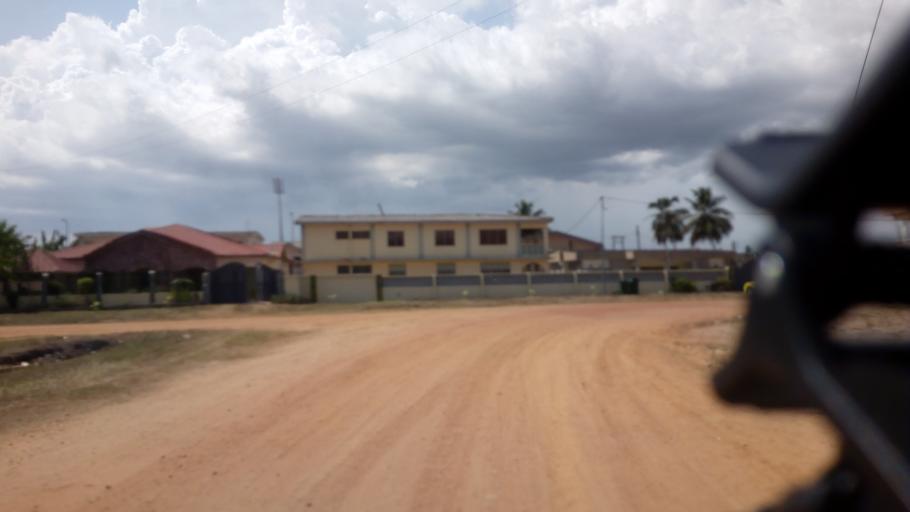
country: GH
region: Central
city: Cape Coast
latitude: 5.1325
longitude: -1.2791
